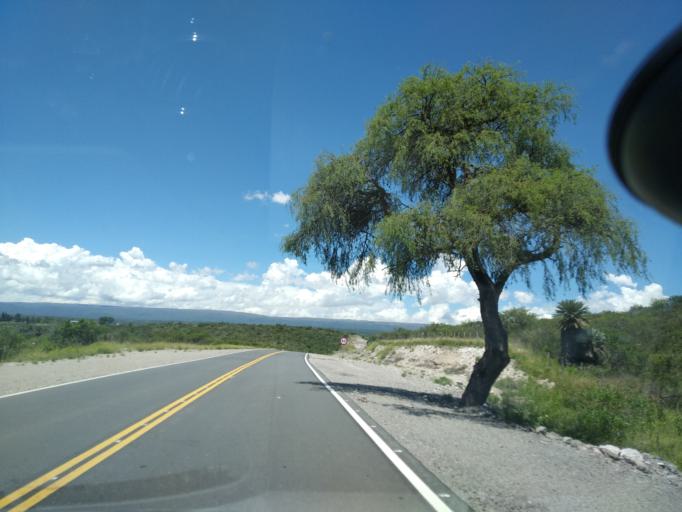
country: AR
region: Cordoba
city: Salsacate
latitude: -31.3460
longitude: -65.0929
